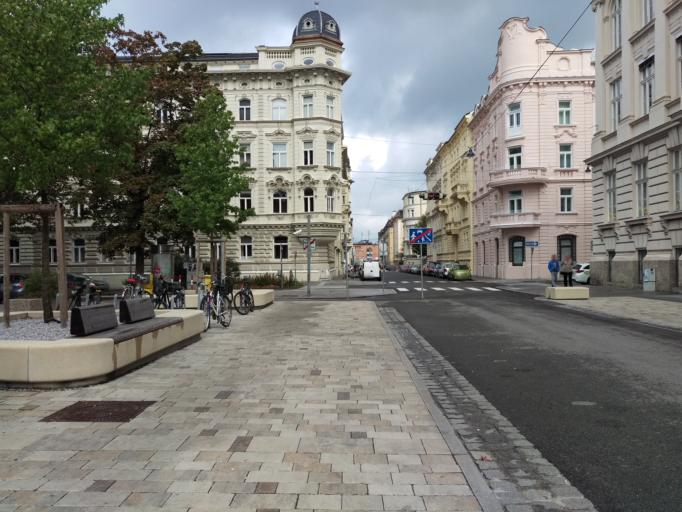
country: AT
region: Salzburg
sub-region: Salzburg Stadt
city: Salzburg
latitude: 47.8063
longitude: 13.0445
